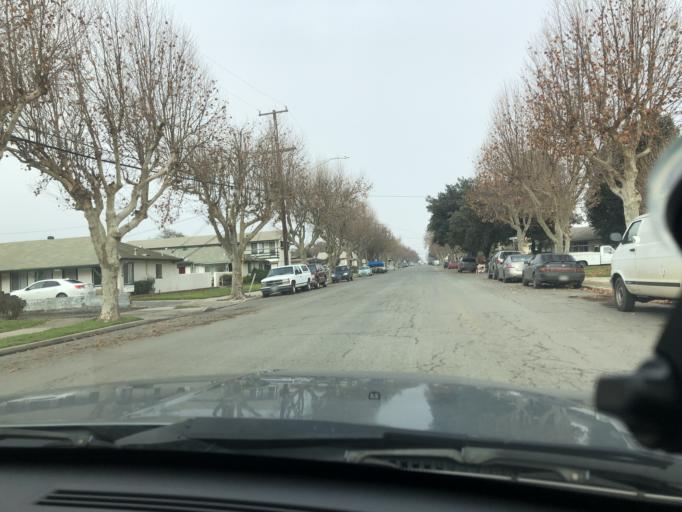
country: US
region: California
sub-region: Monterey County
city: King City
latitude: 36.2099
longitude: -121.1239
